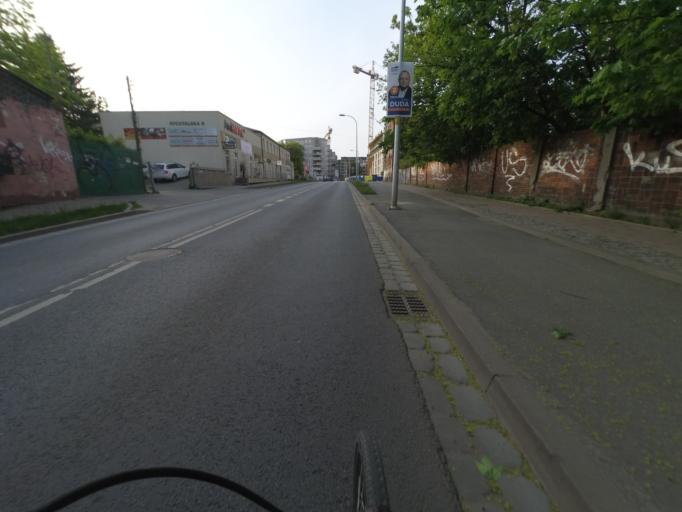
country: PL
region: Lower Silesian Voivodeship
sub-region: Powiat wroclawski
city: Wroclaw
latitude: 51.1283
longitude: 17.0473
